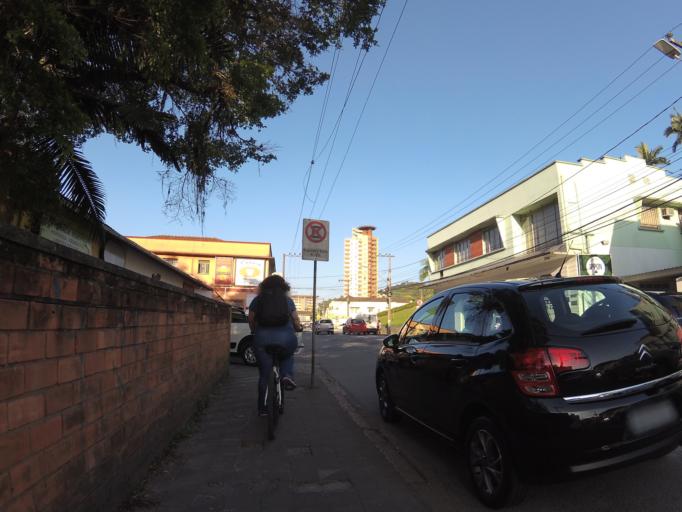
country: BR
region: Santa Catarina
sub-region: Blumenau
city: Blumenau
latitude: -26.9186
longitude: -49.0892
